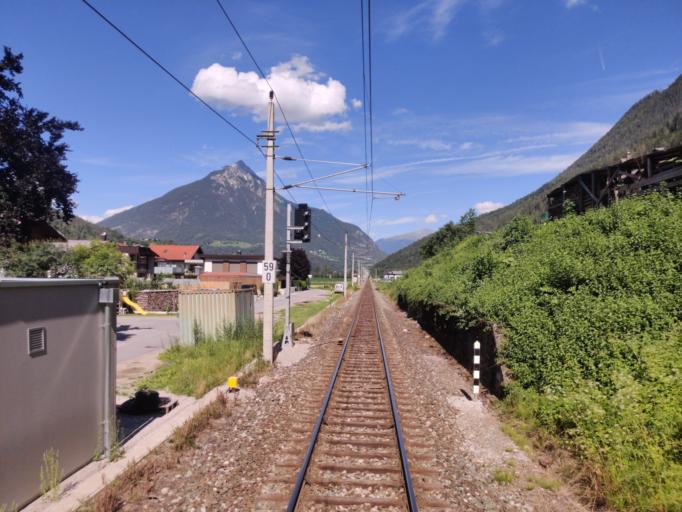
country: AT
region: Tyrol
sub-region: Politischer Bezirk Imst
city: Imsterberg
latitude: 47.2114
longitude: 10.7070
